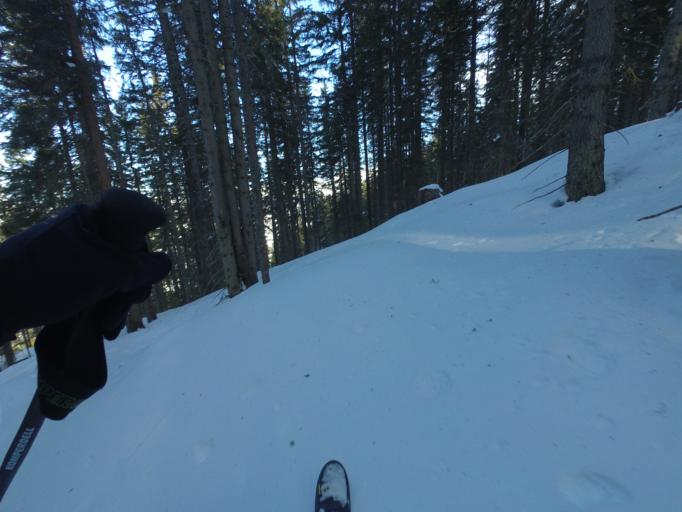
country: AT
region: Salzburg
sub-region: Politischer Bezirk Zell am See
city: Lend
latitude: 47.2706
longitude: 13.0192
